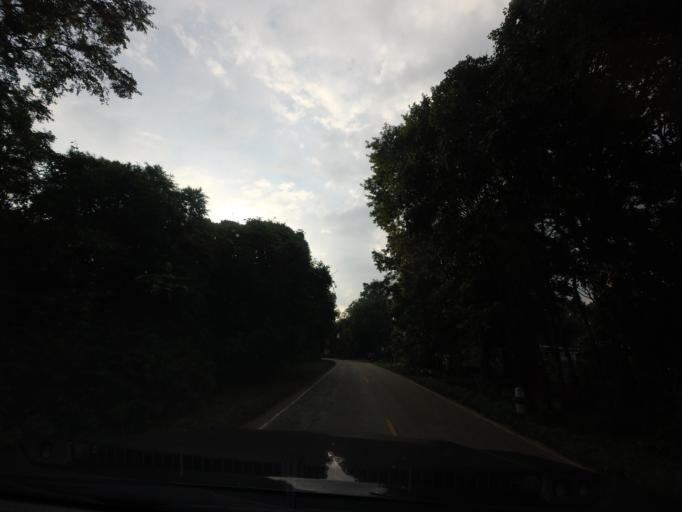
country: TH
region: Loei
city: Dan Sai
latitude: 17.3306
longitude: 101.1116
